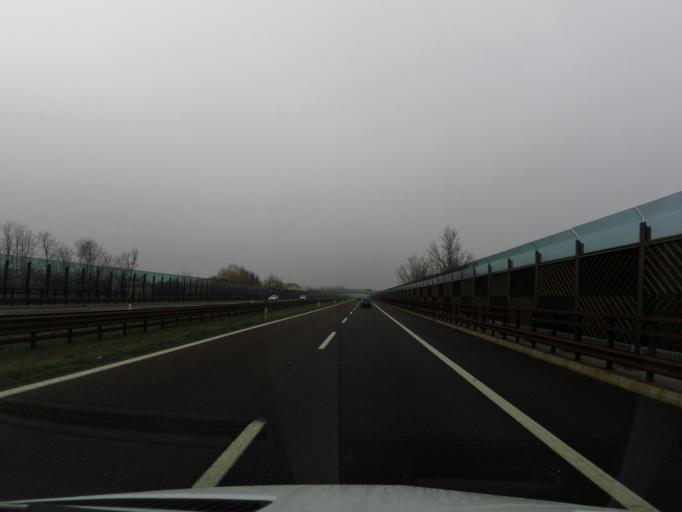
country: IT
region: Emilia-Romagna
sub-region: Provincia di Modena
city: Santa Croce Scuole
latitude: 44.7529
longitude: 10.8448
